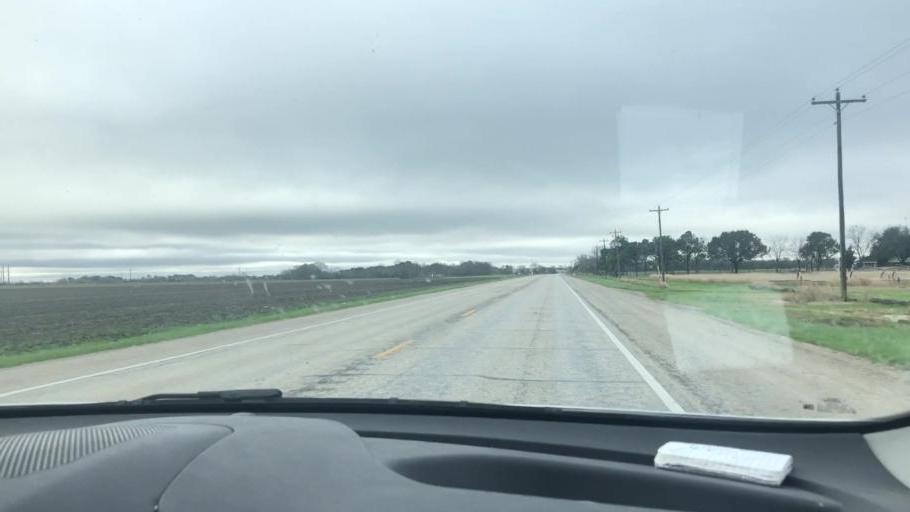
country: US
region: Texas
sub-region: Wharton County
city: Boling
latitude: 29.2234
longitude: -96.0332
